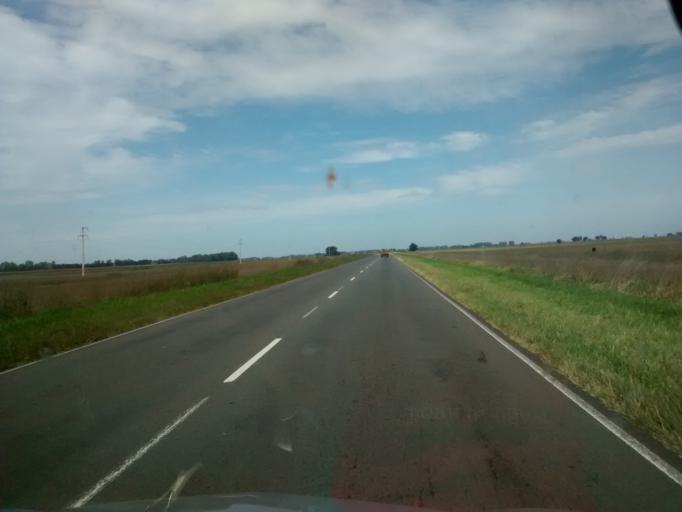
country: AR
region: Buenos Aires
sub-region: Partido de Ayacucho
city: Ayacucho
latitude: -37.0758
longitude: -58.5451
